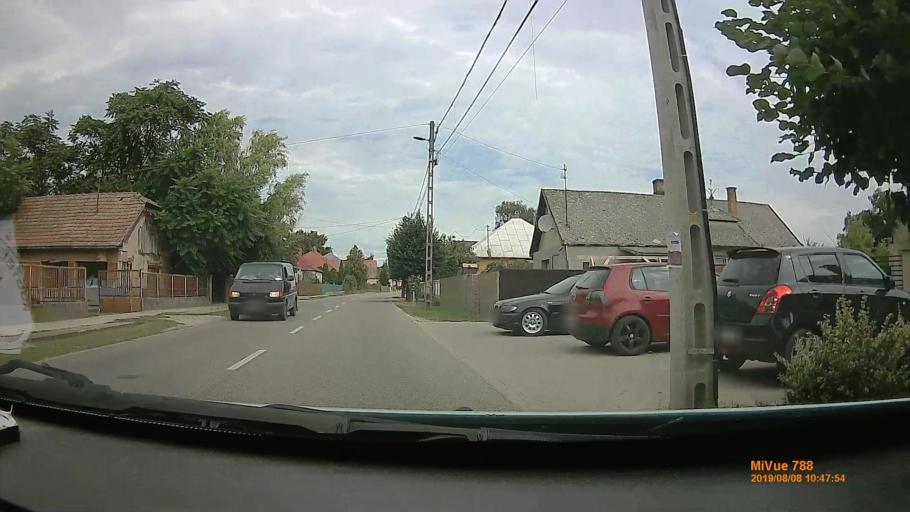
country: HU
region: Szabolcs-Szatmar-Bereg
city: Balkany
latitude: 47.7647
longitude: 21.8630
